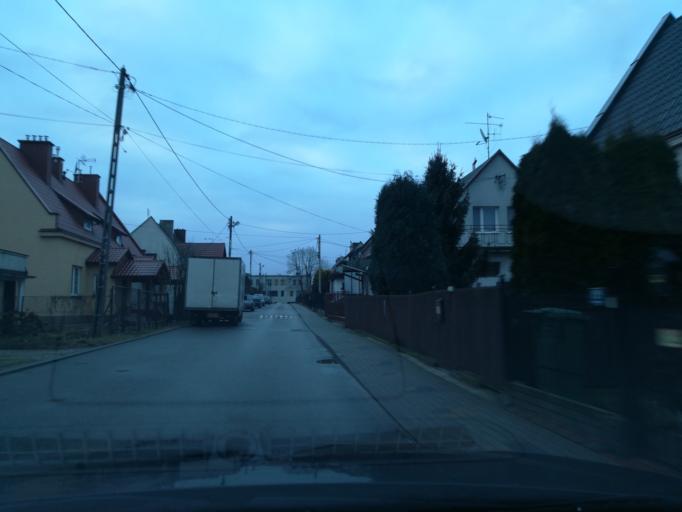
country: PL
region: Subcarpathian Voivodeship
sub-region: Rzeszow
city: Rzeszow
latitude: 50.0164
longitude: 21.9845
